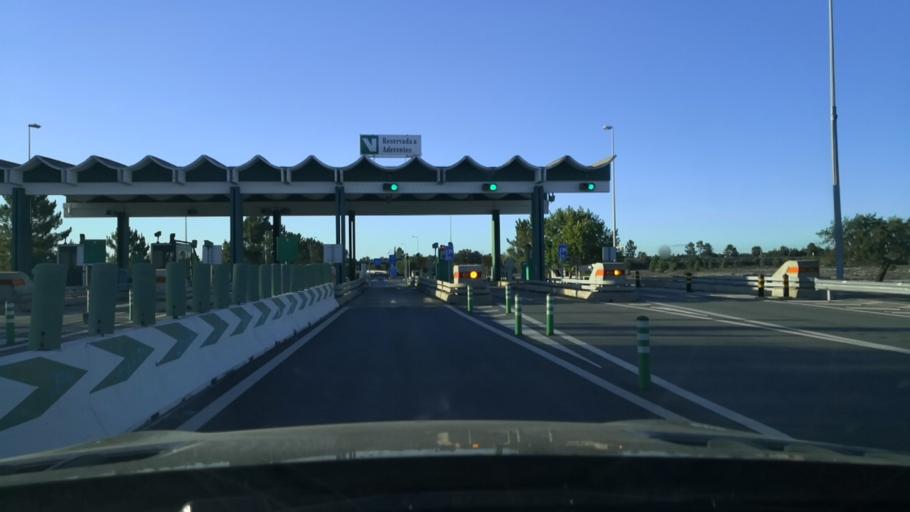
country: PT
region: Setubal
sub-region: Setubal
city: Setubal
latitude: 38.5973
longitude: -8.6735
